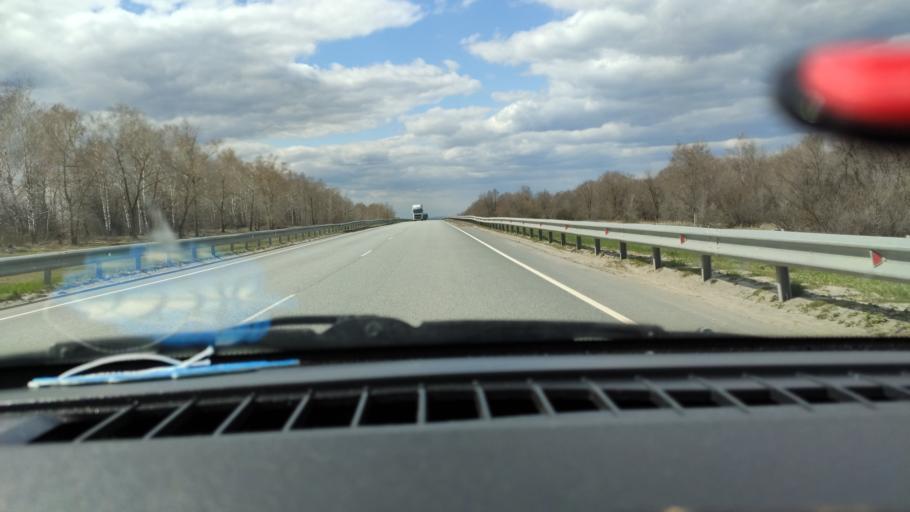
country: RU
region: Saratov
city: Balakovo
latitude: 52.0870
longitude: 47.6849
